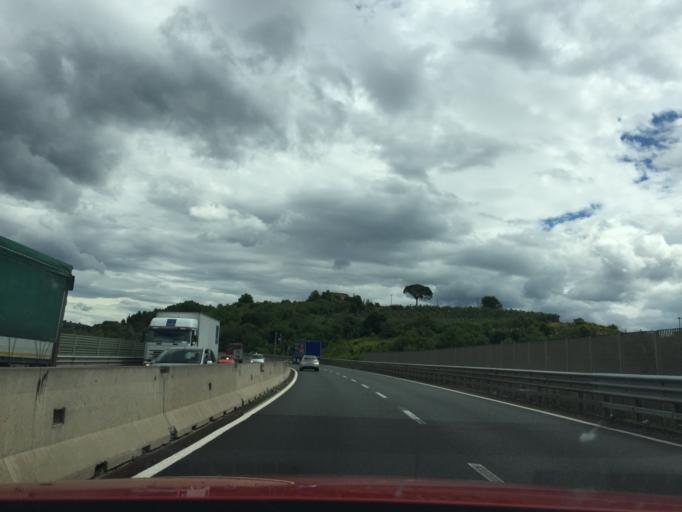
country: IT
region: Tuscany
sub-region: Province of Florence
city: Ginestra Fiorentina
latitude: 43.7120
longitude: 11.0681
